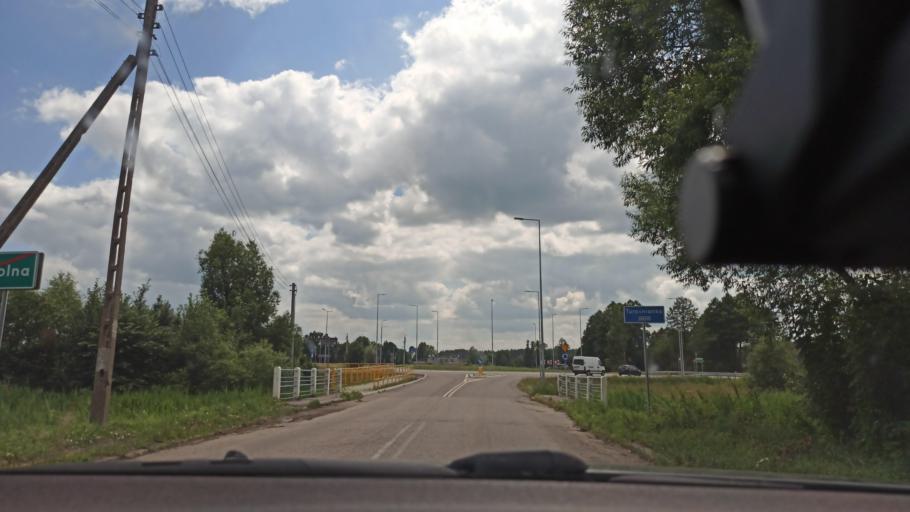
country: PL
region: Podlasie
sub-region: Powiat bialostocki
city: Turosn Koscielna
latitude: 53.0175
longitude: 23.0023
